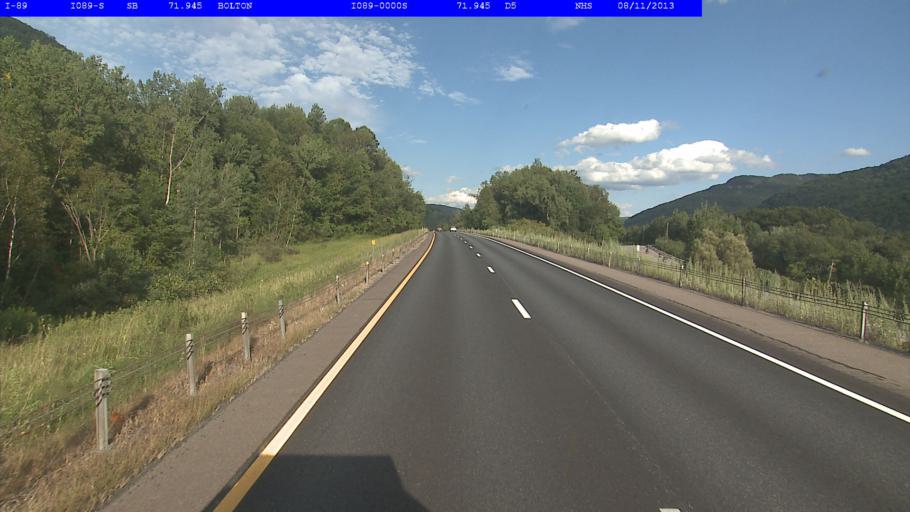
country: US
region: Vermont
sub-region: Washington County
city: Waterbury
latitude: 44.3785
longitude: -72.9054
